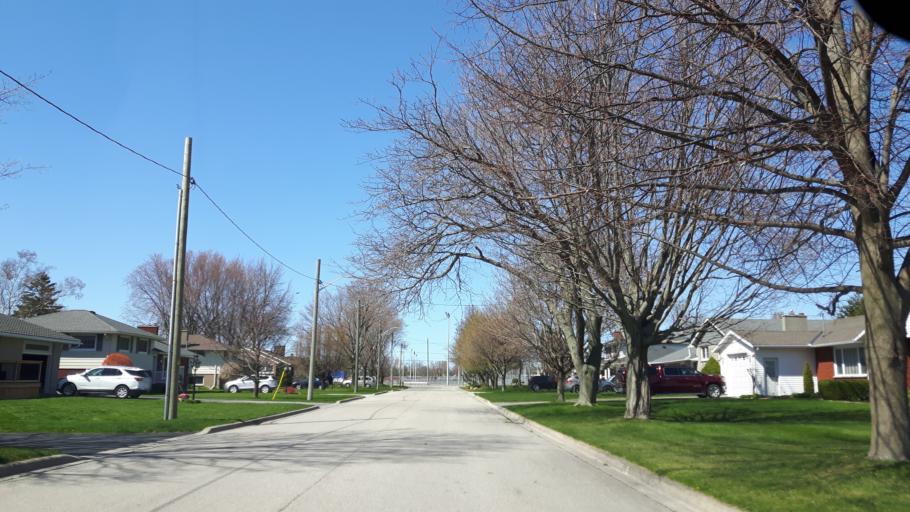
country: CA
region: Ontario
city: Goderich
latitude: 43.7339
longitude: -81.7153
